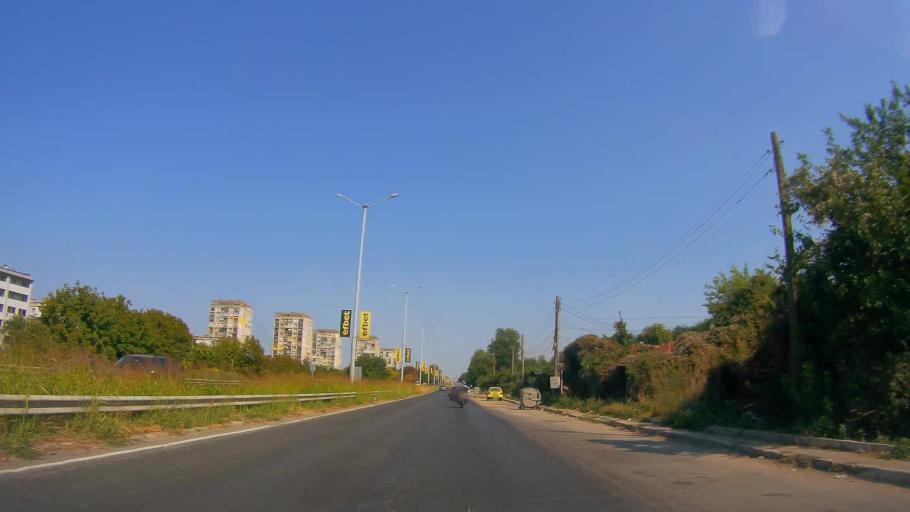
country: BG
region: Ruse
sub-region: Obshtina Ruse
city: Ruse
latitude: 43.8417
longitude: 25.9769
